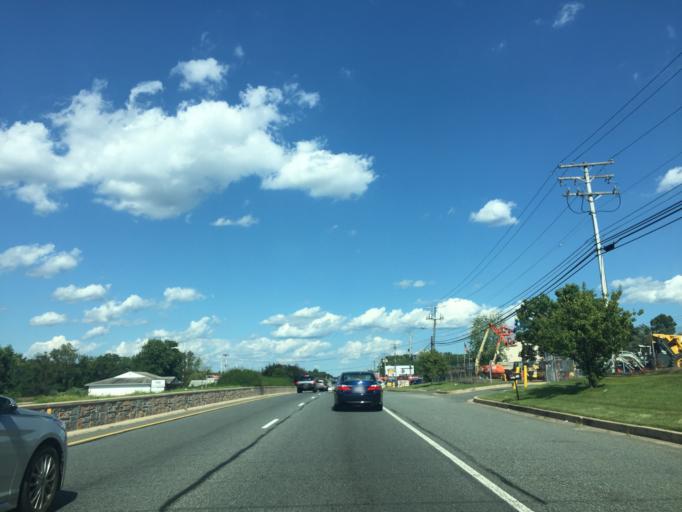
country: US
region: Maryland
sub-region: Harford County
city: Joppatowne
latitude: 39.4283
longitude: -76.3604
